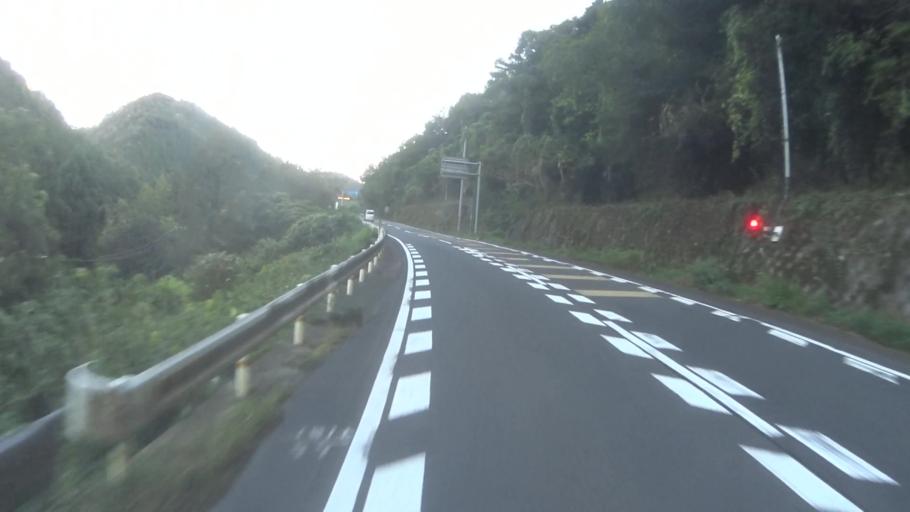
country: JP
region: Kyoto
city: Ayabe
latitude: 35.2882
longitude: 135.2651
